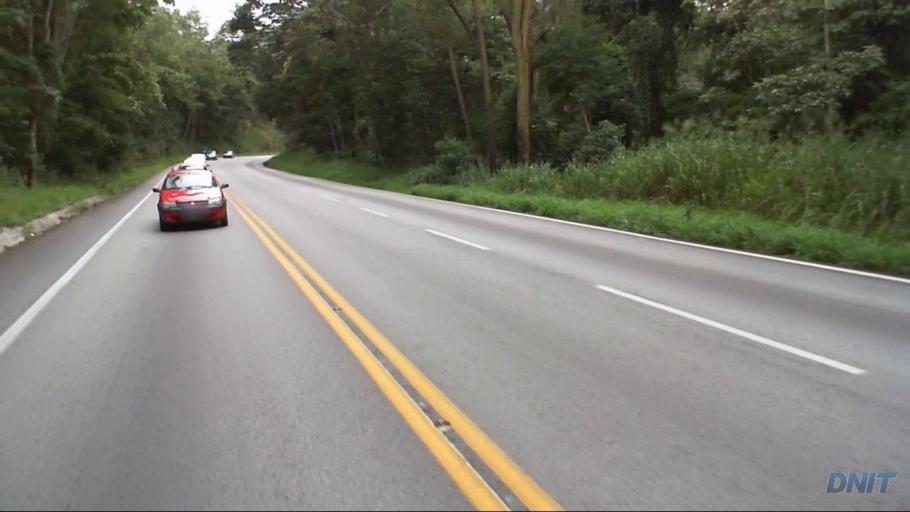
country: BR
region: Minas Gerais
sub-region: Joao Monlevade
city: Joao Monlevade
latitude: -19.8485
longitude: -43.1090
